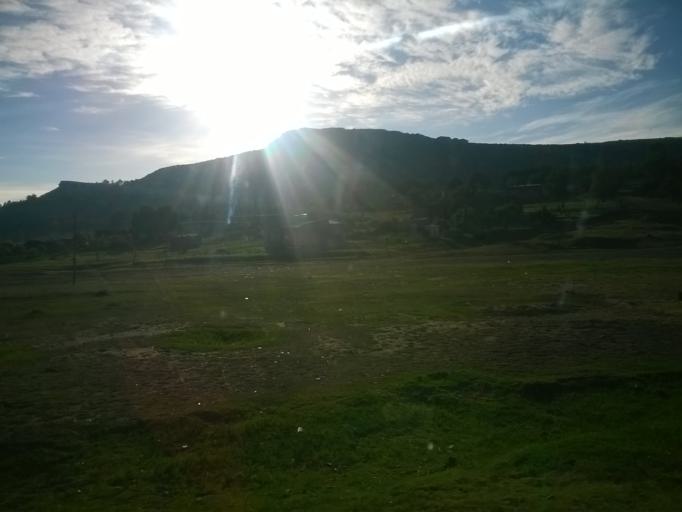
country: LS
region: Maseru
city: Maseru
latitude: -29.2452
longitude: 27.6051
